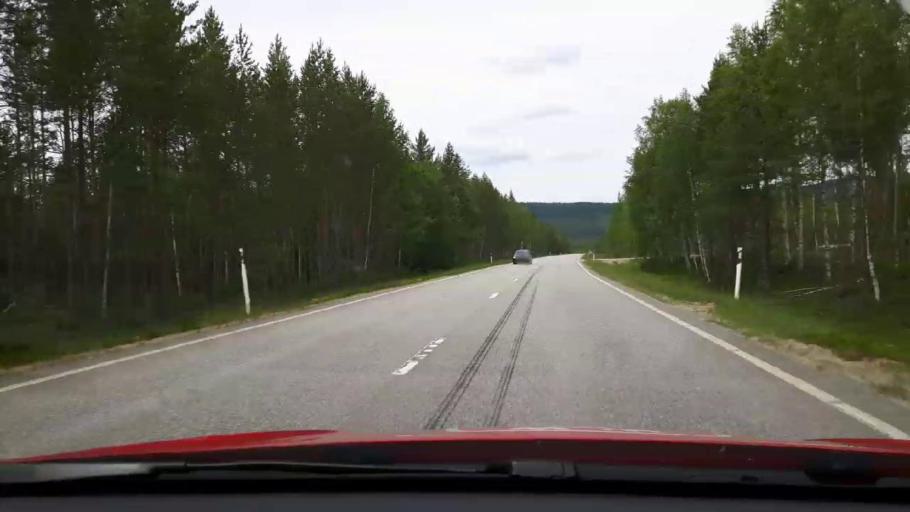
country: SE
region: Jaemtland
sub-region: Harjedalens Kommun
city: Sveg
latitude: 62.0833
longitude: 14.2543
